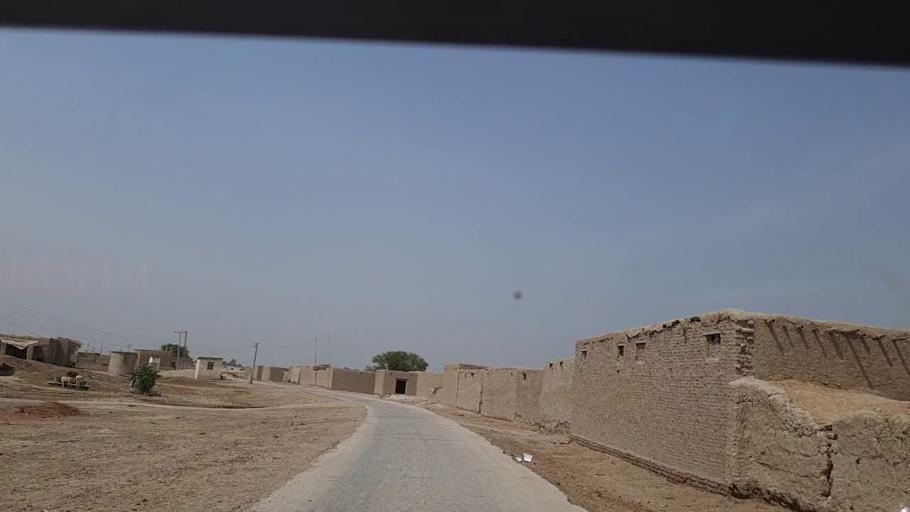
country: PK
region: Sindh
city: Khairpur Nathan Shah
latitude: 27.0676
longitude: 67.6506
